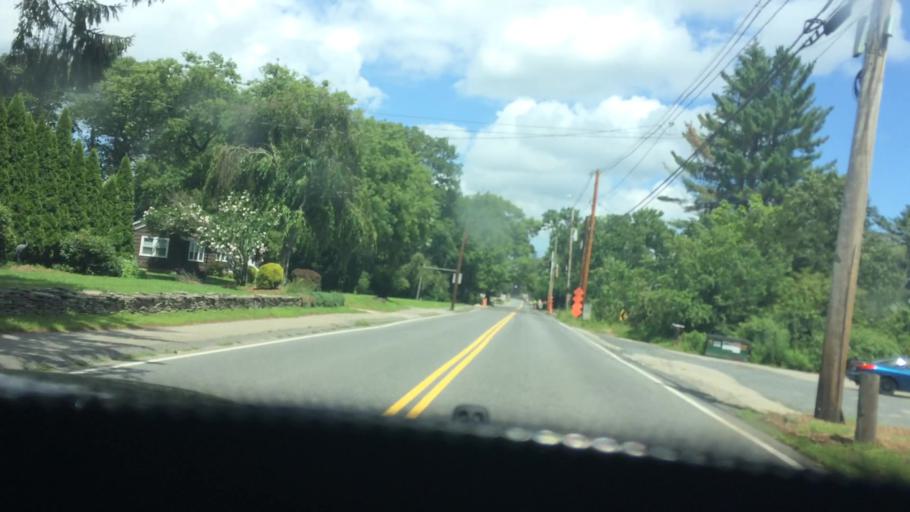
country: US
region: Massachusetts
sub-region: Middlesex County
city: Maynard
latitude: 42.4153
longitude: -71.4464
